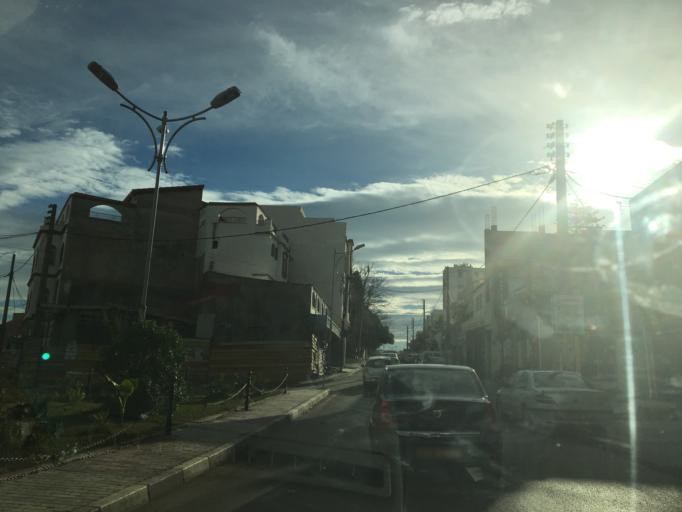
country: DZ
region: Alger
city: Birkhadem
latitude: 36.7359
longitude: 3.0960
